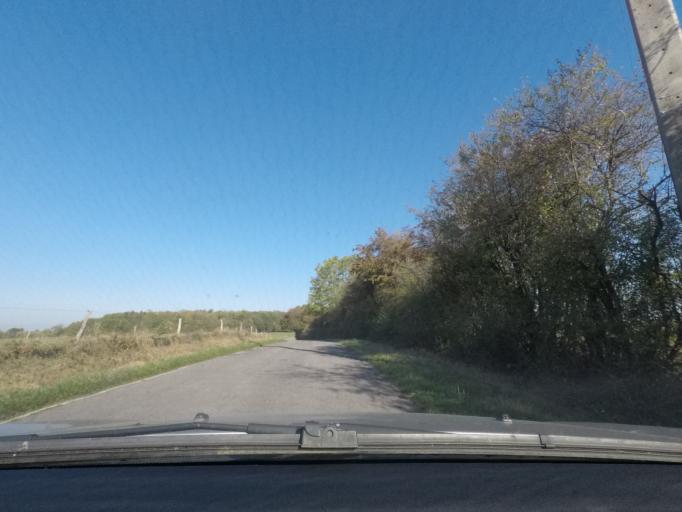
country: BE
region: Wallonia
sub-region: Province du Luxembourg
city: Etalle
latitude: 49.7015
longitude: 5.5689
